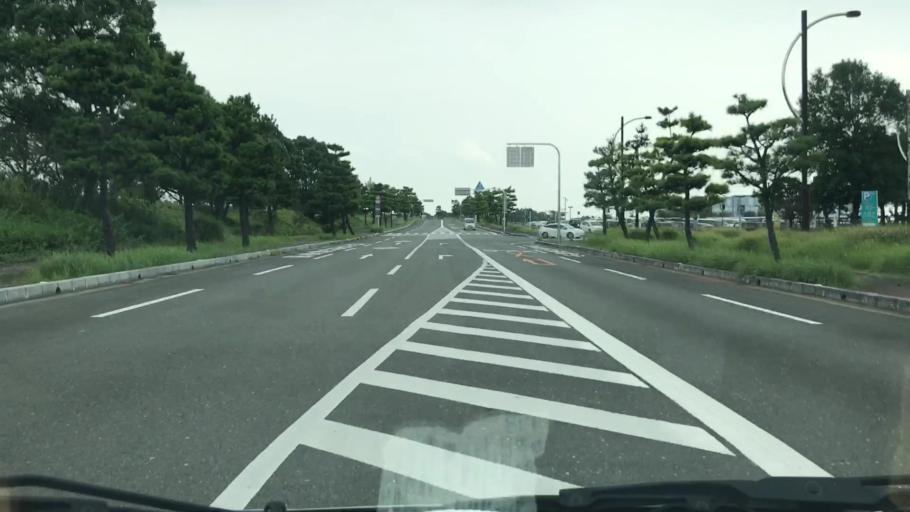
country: JP
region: Saga Prefecture
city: Okawa
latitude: 33.1544
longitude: 130.3041
